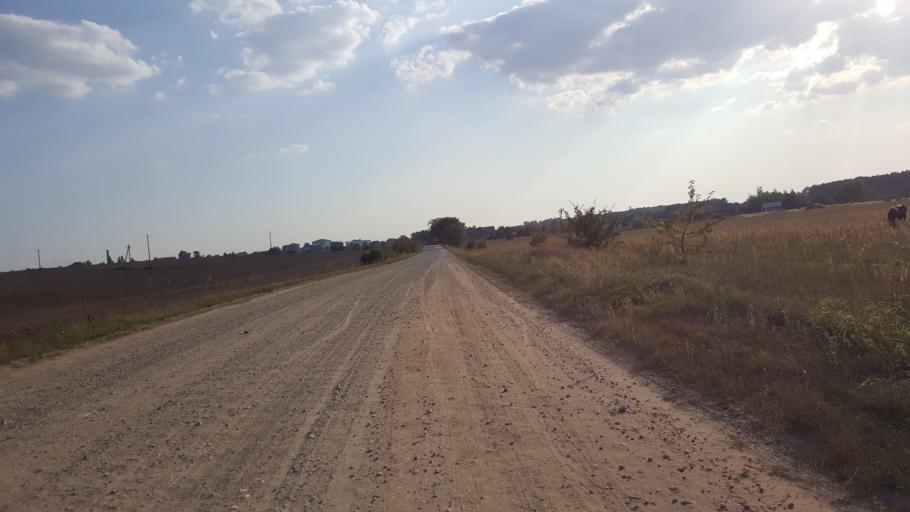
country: BY
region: Brest
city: Kamyanyets
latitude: 52.4143
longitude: 23.8388
